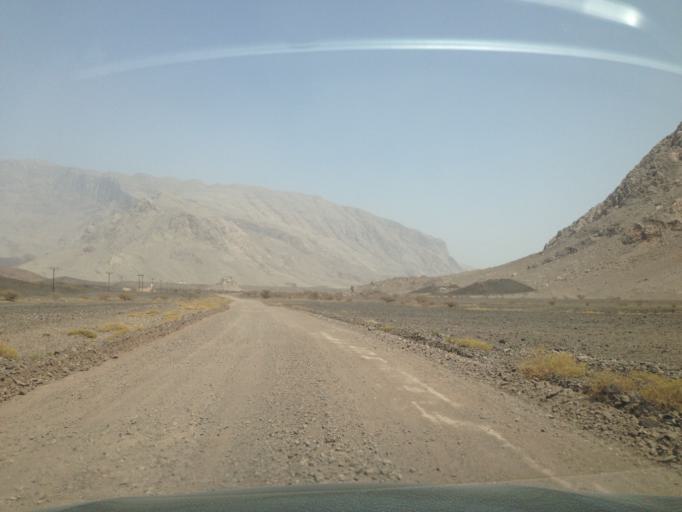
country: OM
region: Az Zahirah
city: `Ibri
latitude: 23.1892
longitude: 56.8905
